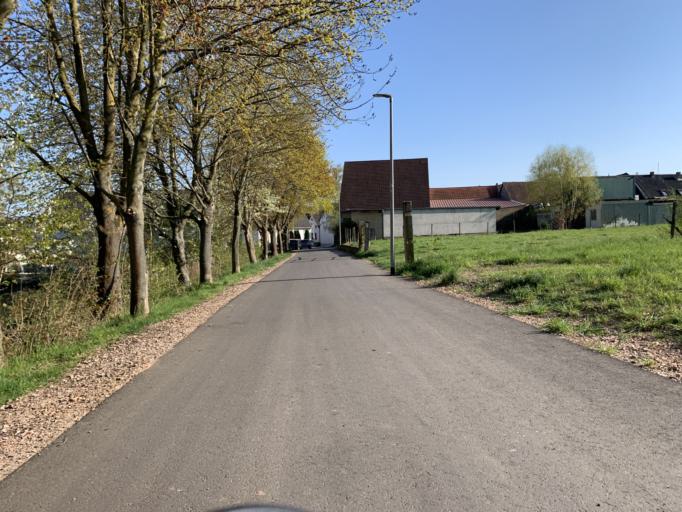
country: DE
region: Rheinland-Pfalz
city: Windesheim
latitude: 49.8980
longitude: 7.8333
